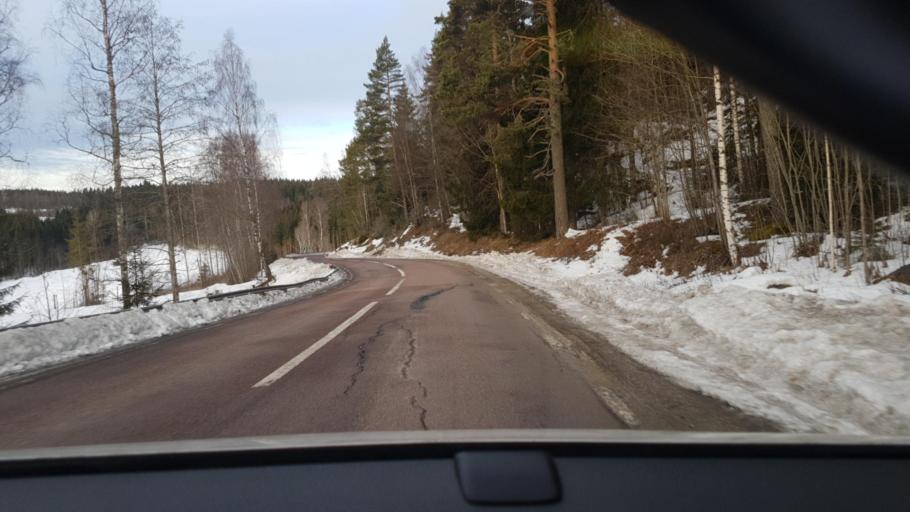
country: SE
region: Vaermland
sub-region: Eda Kommun
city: Amotfors
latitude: 59.7654
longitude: 12.2562
